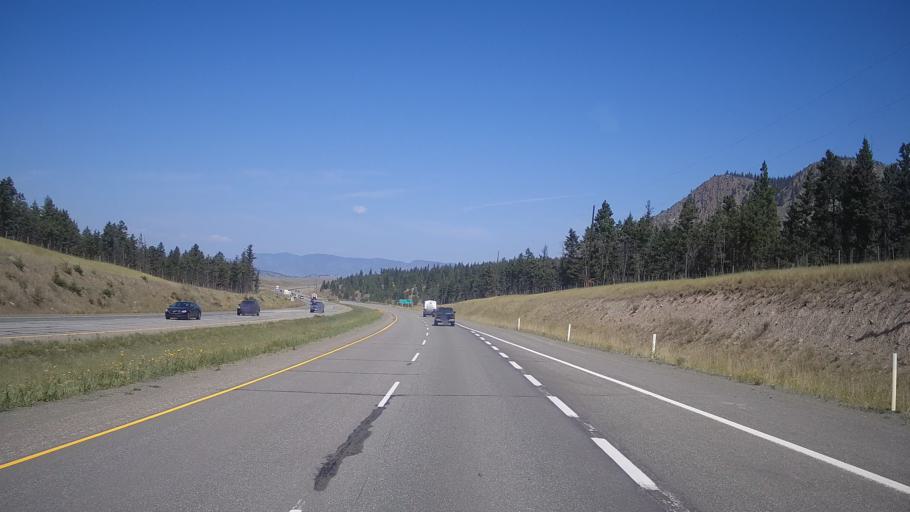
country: CA
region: British Columbia
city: Kamloops
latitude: 50.6234
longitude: -120.4724
